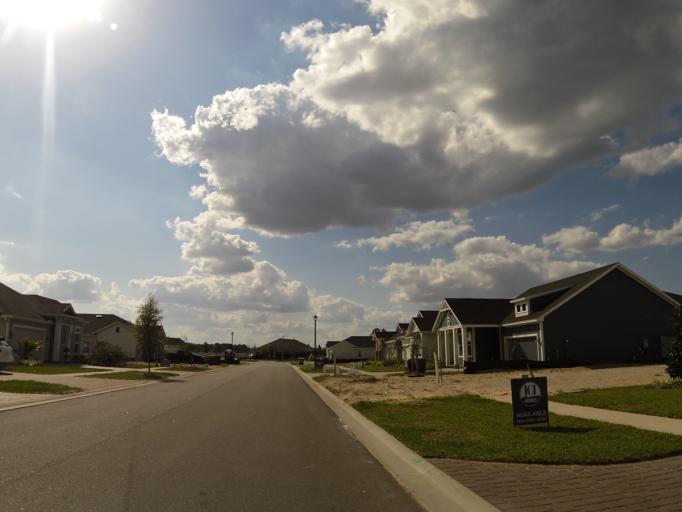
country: US
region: Florida
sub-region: Saint Johns County
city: Palm Valley
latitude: 30.1754
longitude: -81.5037
